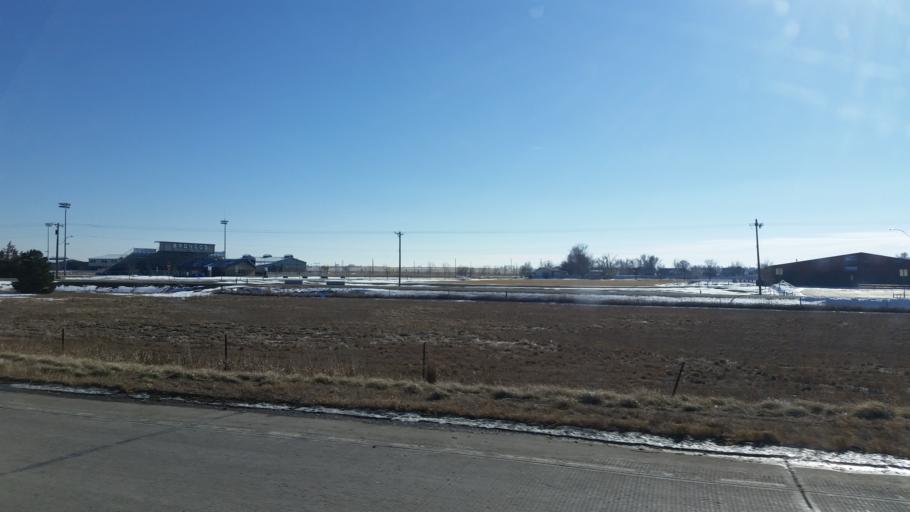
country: US
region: Colorado
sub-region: Weld County
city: Kersey
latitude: 40.3929
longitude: -104.5564
